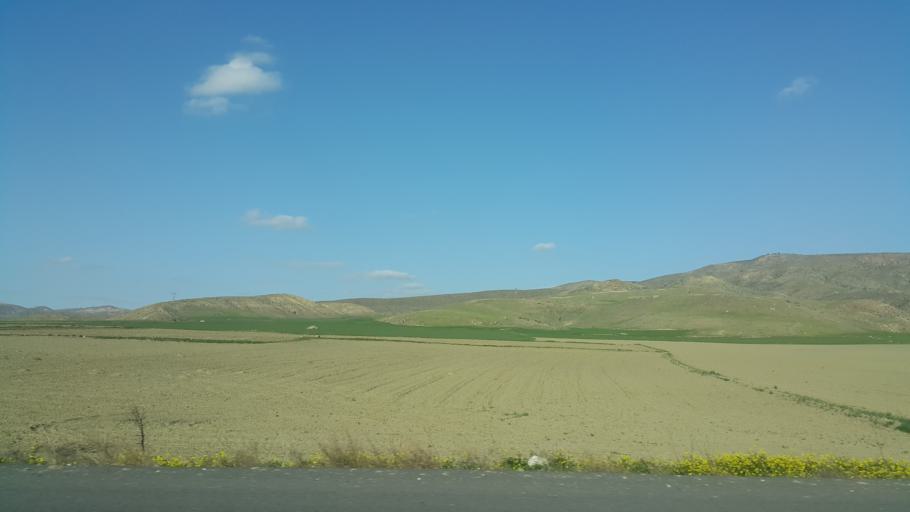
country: TR
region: Ankara
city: Sereflikochisar
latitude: 38.8338
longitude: 33.5928
